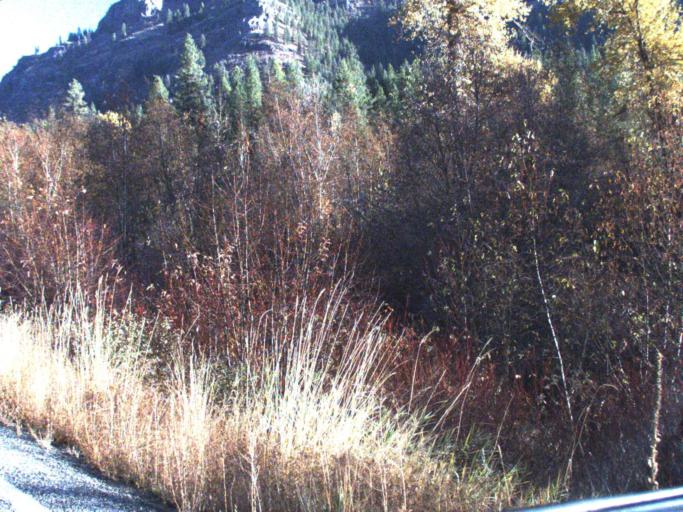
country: US
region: Washington
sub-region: Ferry County
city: Republic
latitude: 48.3301
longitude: -118.7461
